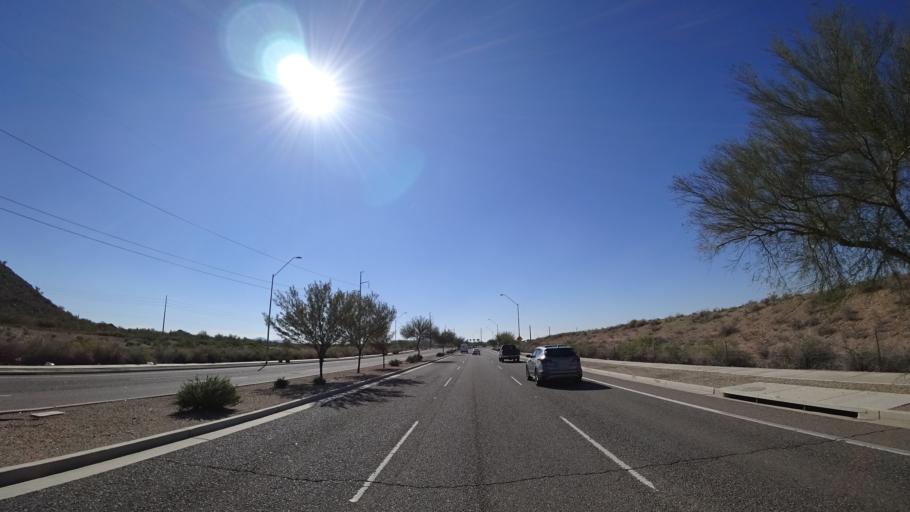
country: US
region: Arizona
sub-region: Maricopa County
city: Cave Creek
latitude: 33.6861
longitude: -112.0520
